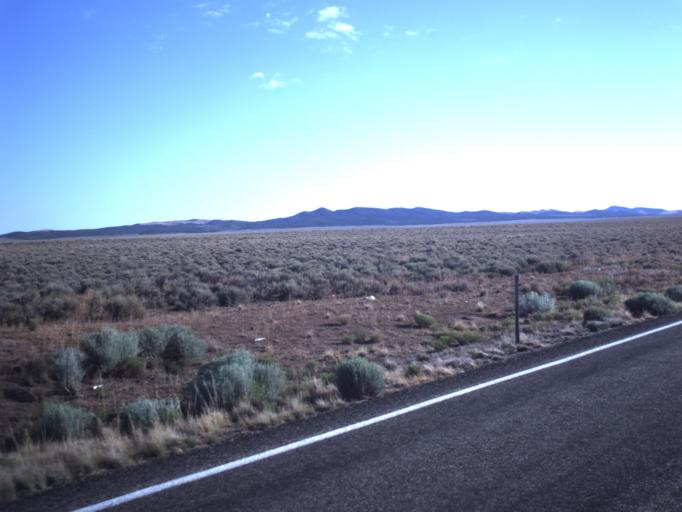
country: US
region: Utah
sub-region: Iron County
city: Enoch
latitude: 37.9308
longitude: -113.0288
